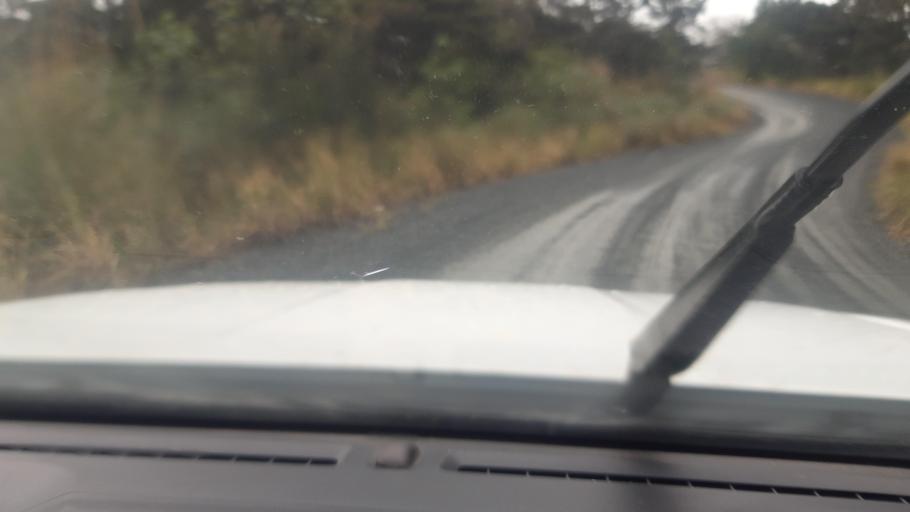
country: NZ
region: Northland
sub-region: Far North District
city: Kaitaia
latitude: -35.0019
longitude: 173.2149
